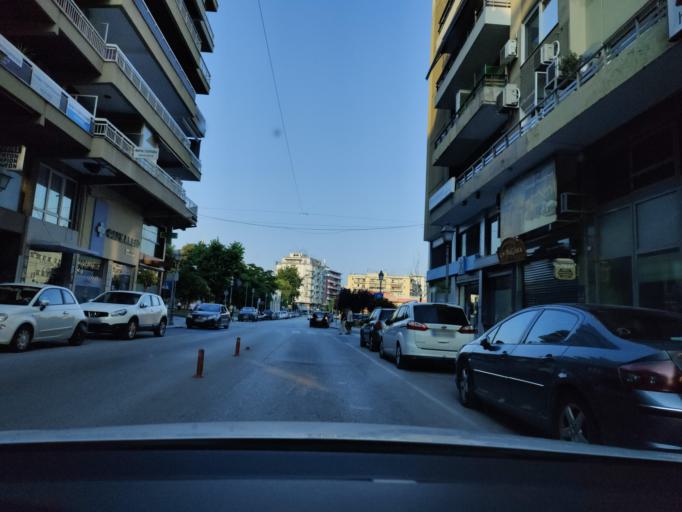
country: GR
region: East Macedonia and Thrace
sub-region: Nomos Kavalas
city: Kavala
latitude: 40.9369
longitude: 24.4064
